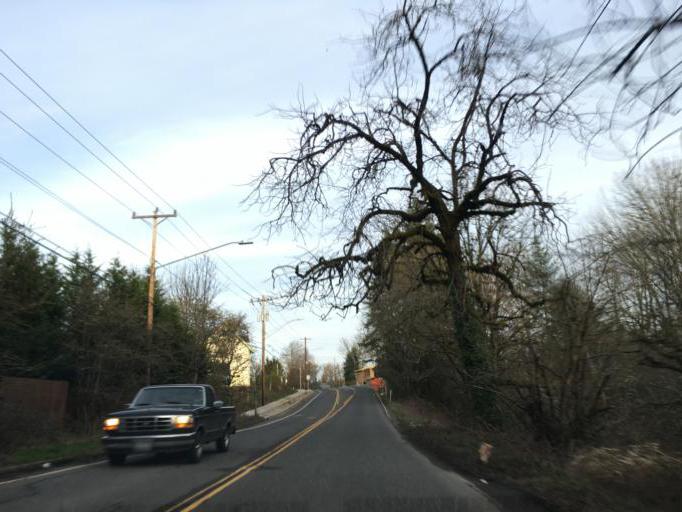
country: US
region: Oregon
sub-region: Clackamas County
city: Lake Oswego
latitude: 45.4392
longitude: -122.6888
